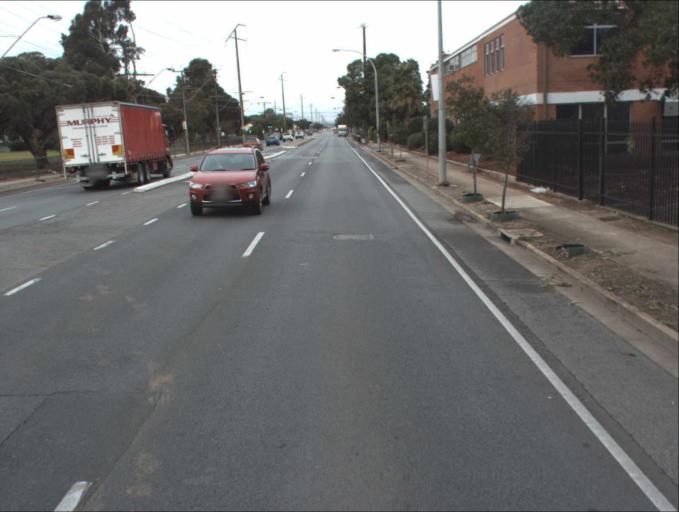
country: AU
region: South Australia
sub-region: Port Adelaide Enfield
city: Blair Athol
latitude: -34.8554
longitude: 138.5827
